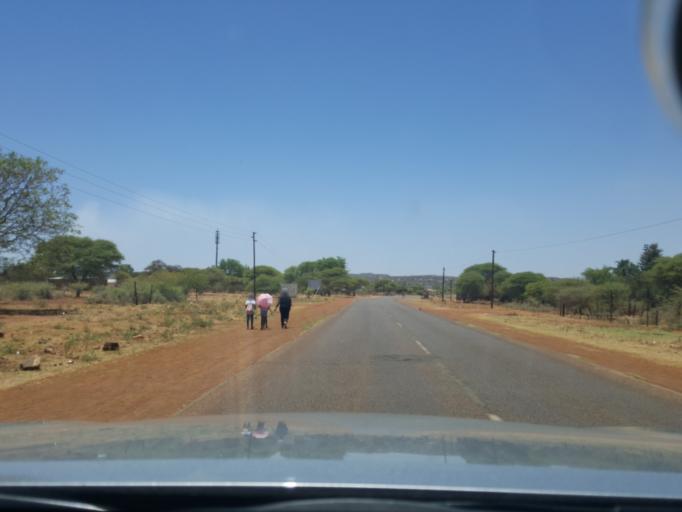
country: ZA
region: North-West
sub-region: Ngaka Modiri Molema District Municipality
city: Zeerust
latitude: -25.4270
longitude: 25.9581
